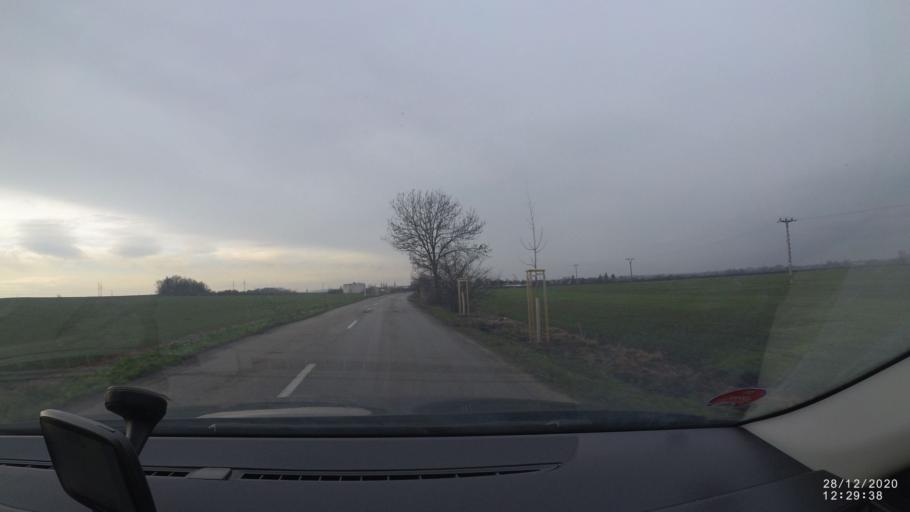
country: CZ
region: Central Bohemia
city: Kostelec nad Labem
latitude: 50.1978
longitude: 14.6098
